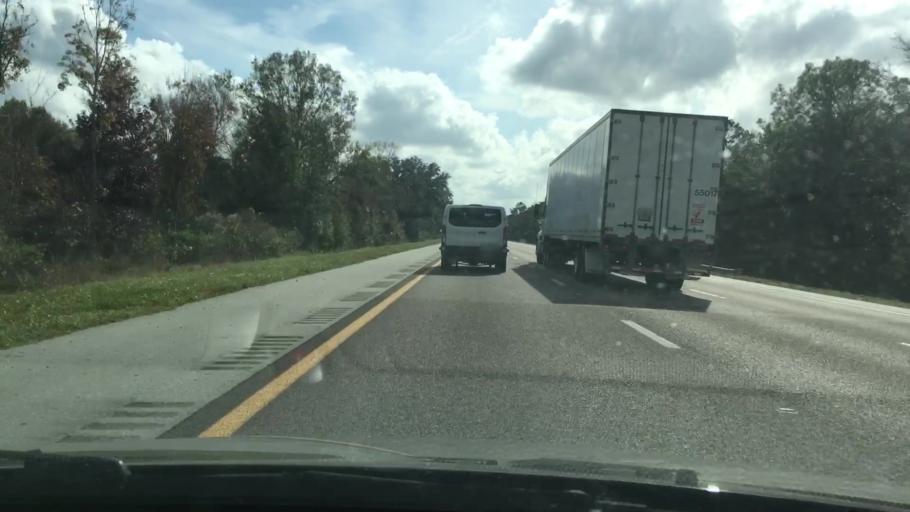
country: US
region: Florida
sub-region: Volusia County
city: Oak Hill
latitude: 28.8643
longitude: -80.9188
